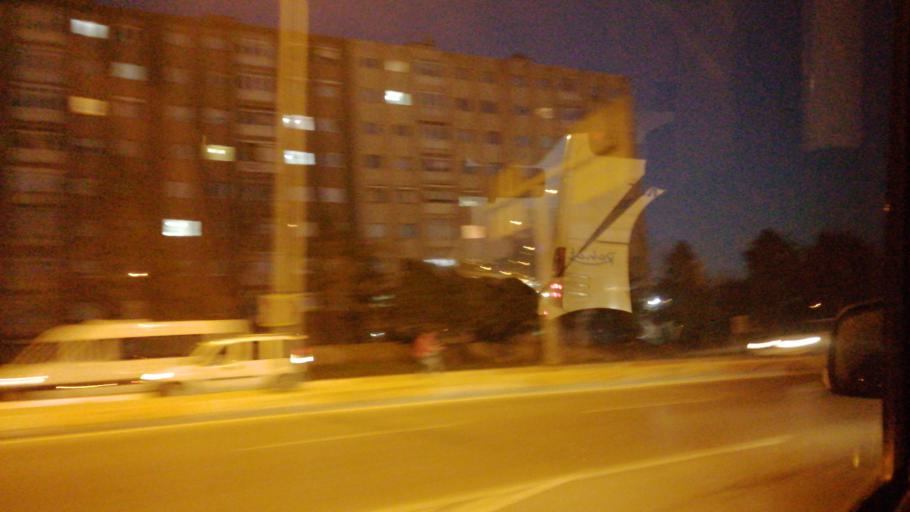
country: TR
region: Istanbul
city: Umraniye
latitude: 40.9934
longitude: 29.1551
